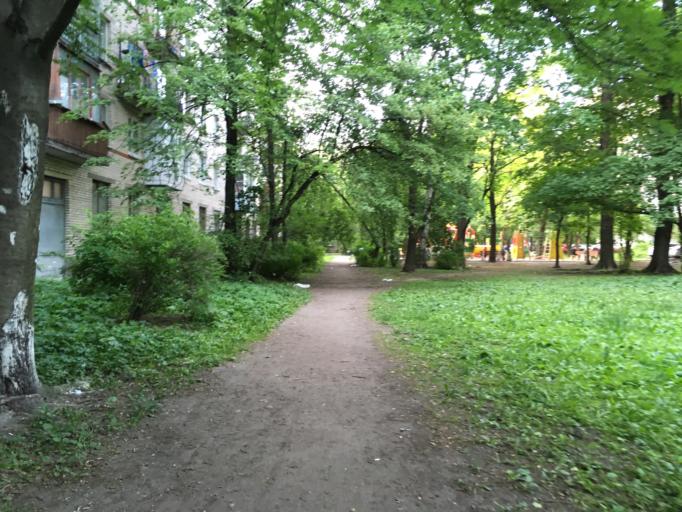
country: RU
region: St.-Petersburg
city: Kushelevka
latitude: 59.9956
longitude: 30.3551
